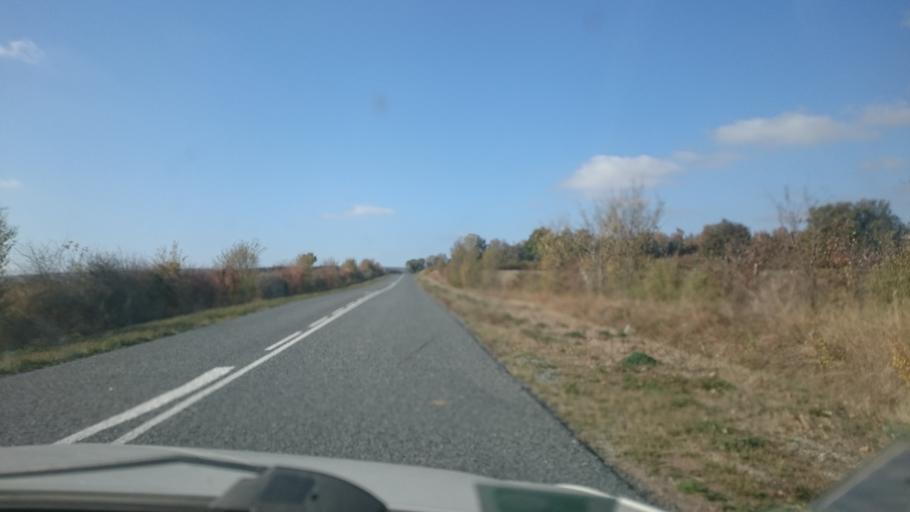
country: FR
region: Auvergne
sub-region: Departement de l'Allier
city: Souvigny
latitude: 46.5264
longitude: 3.1677
